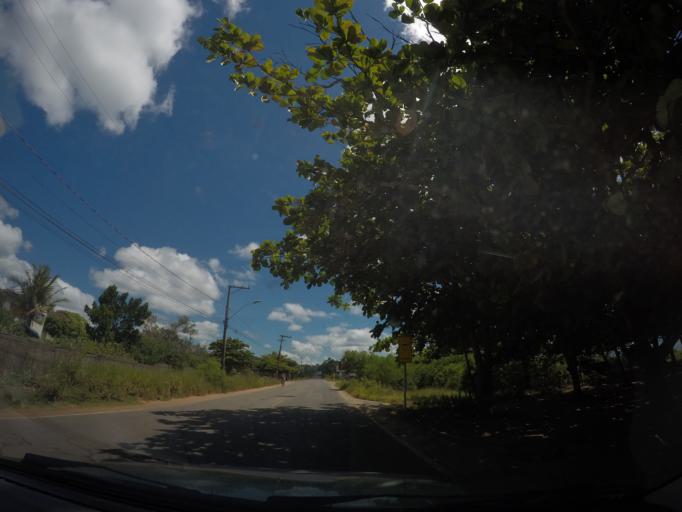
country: BR
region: Espirito Santo
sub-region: Serra
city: Serra
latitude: -20.0136
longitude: -40.1573
